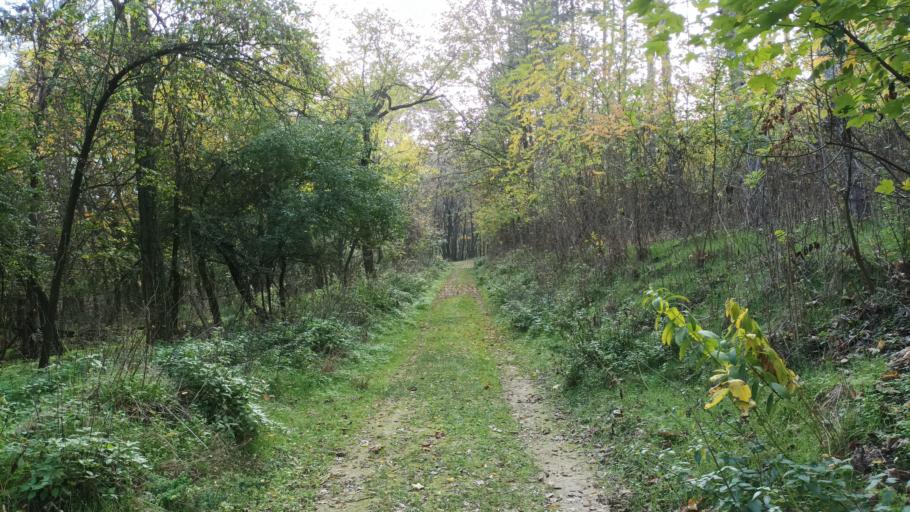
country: HU
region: Tolna
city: Szentgalpuszta
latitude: 46.3502
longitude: 18.6141
